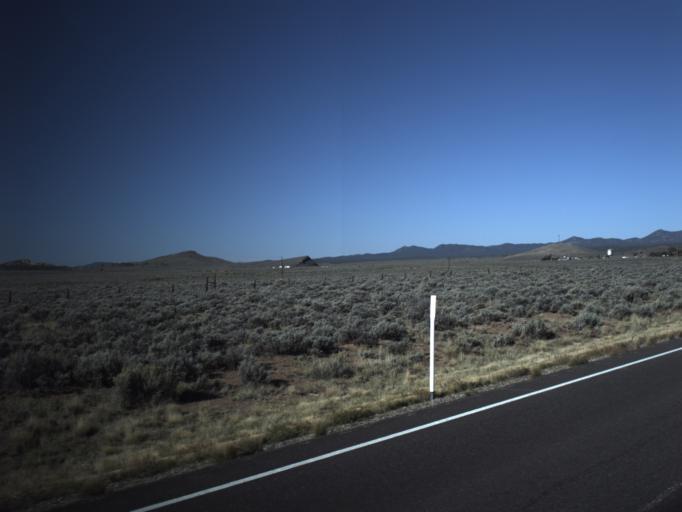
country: US
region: Utah
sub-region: Washington County
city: Enterprise
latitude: 37.7971
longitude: -113.9066
